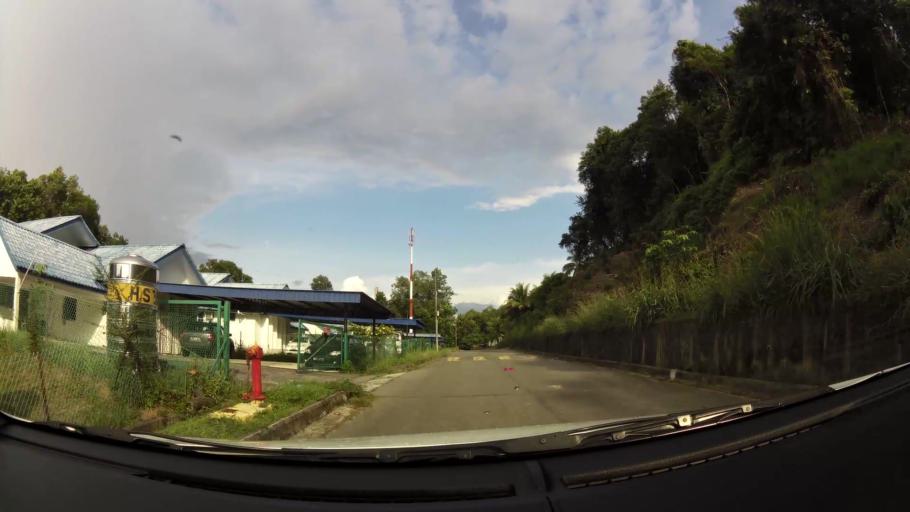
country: BN
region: Brunei and Muara
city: Bandar Seri Begawan
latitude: 4.9650
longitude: 114.9832
